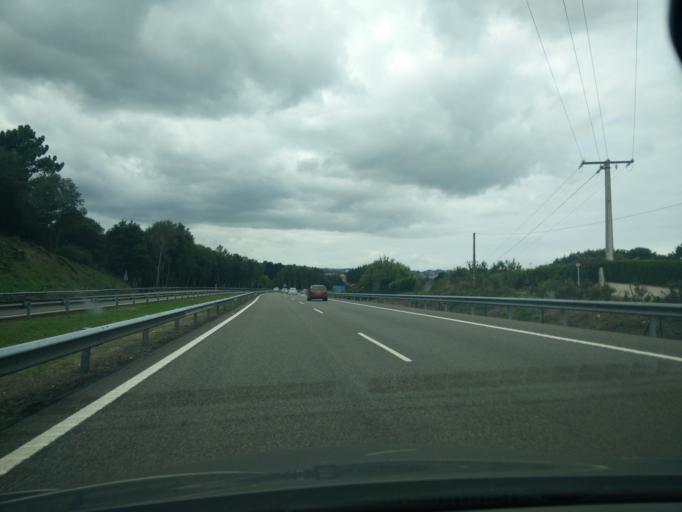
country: ES
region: Galicia
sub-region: Provincia da Coruna
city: Cambre
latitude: 43.3070
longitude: -8.3426
